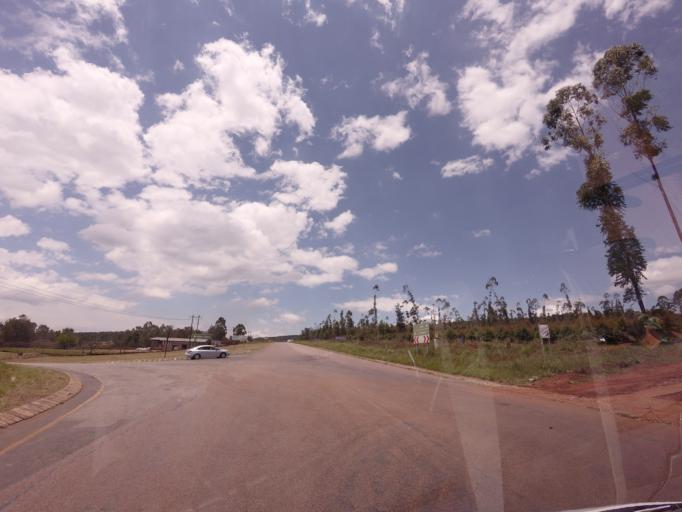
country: ZA
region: Mpumalanga
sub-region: Ehlanzeni District
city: Graksop
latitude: -25.0829
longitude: 30.7887
